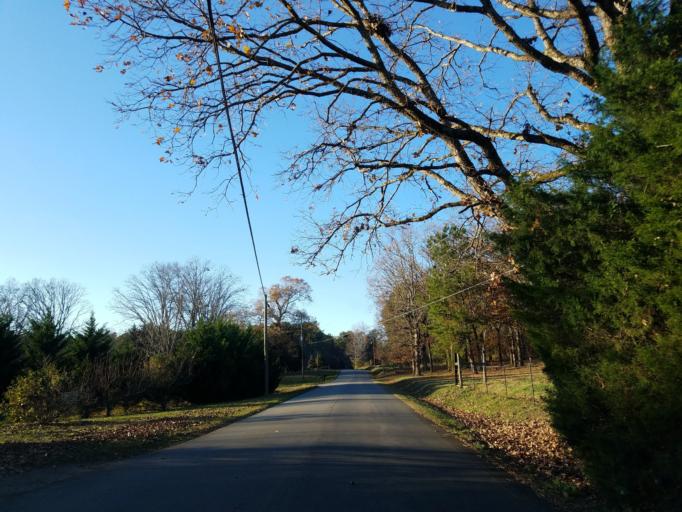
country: US
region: Georgia
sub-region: Pickens County
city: Nelson
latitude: 34.3613
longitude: -84.3693
